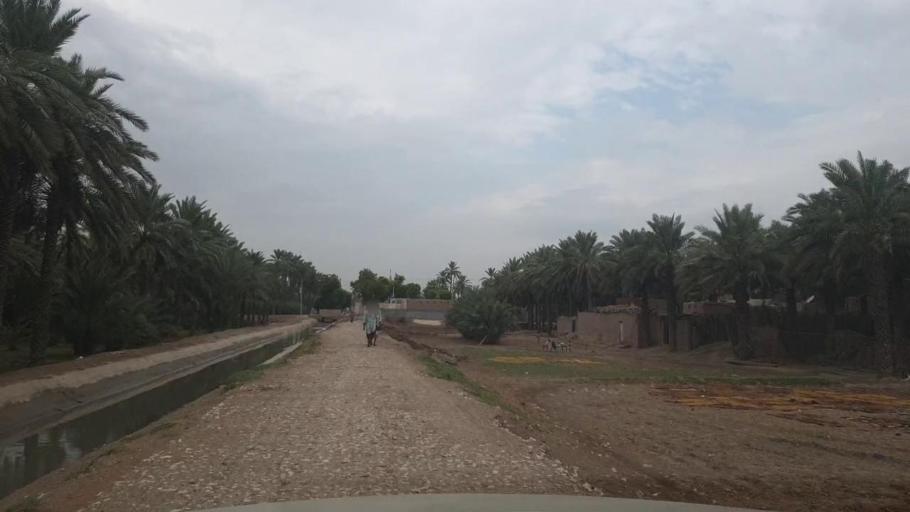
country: PK
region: Sindh
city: Sukkur
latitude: 27.6248
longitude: 68.8201
